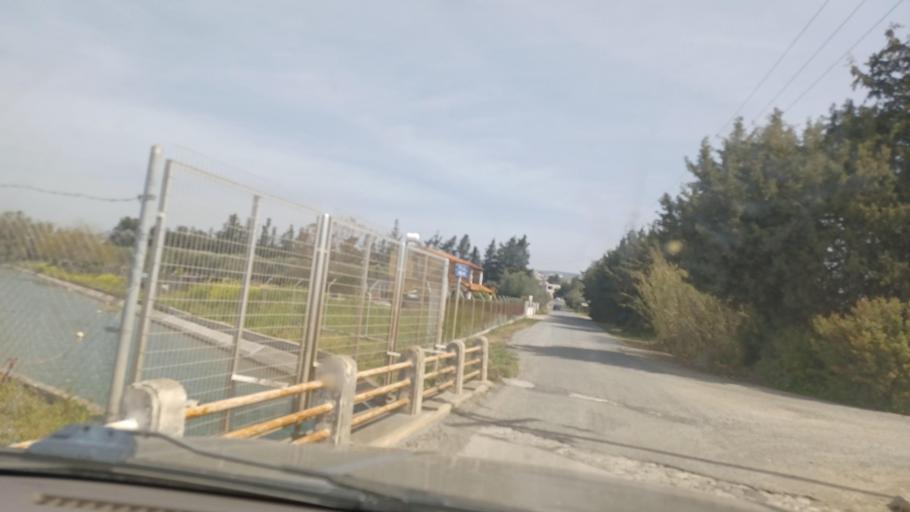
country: CY
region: Pafos
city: Paphos
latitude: 34.7470
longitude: 32.4625
